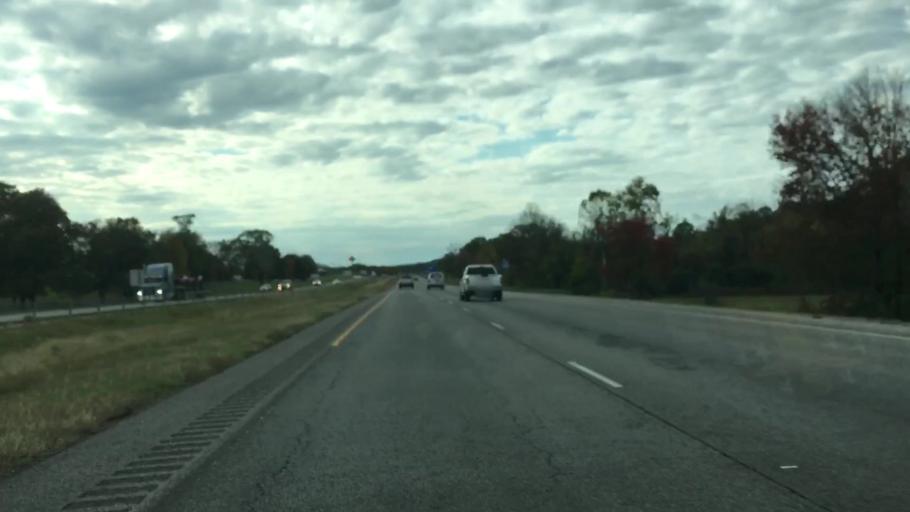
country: US
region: Arkansas
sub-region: Conway County
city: Morrilton
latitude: 35.1743
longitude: -92.7249
